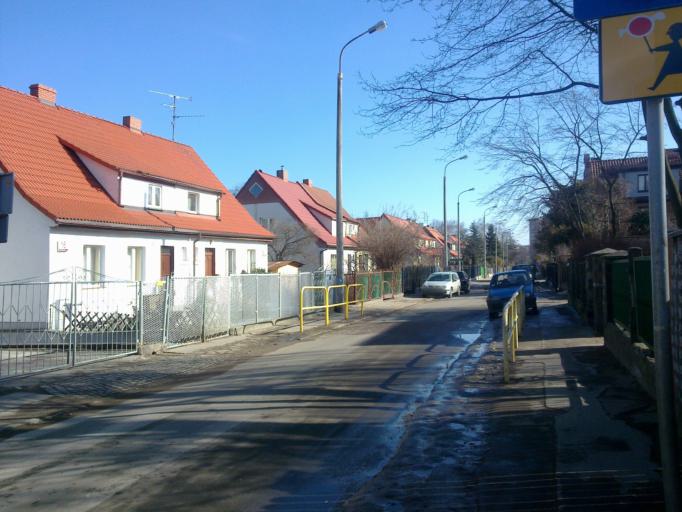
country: PL
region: Pomeranian Voivodeship
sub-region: Gdansk
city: Gdansk
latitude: 54.3856
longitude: 18.6175
